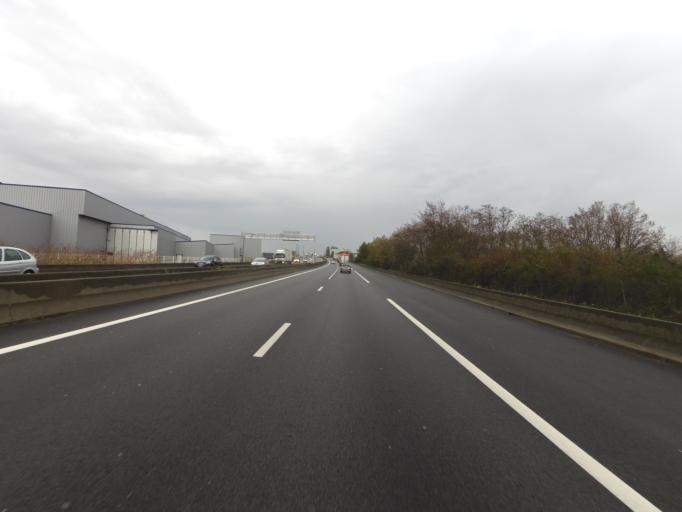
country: FR
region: Rhone-Alpes
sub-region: Departement du Rhone
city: Chassieu
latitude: 45.7202
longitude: 4.9725
